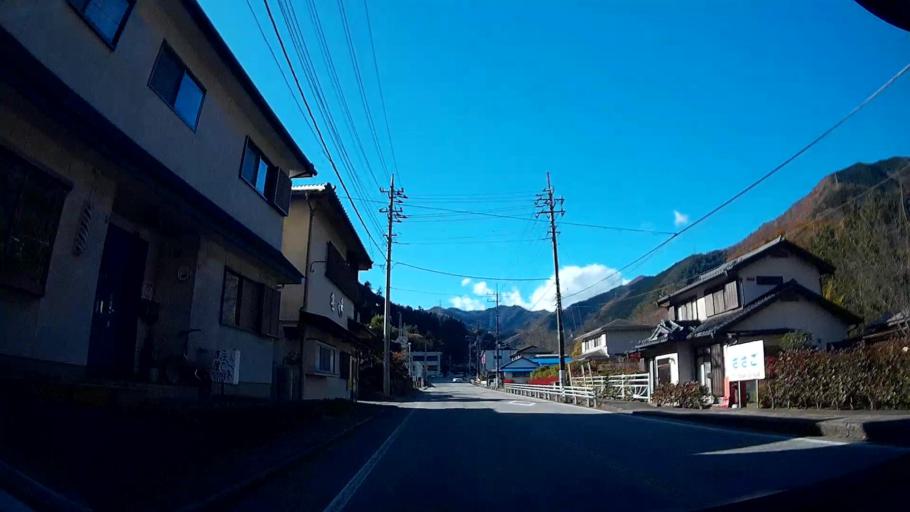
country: JP
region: Yamanashi
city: Otsuki
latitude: 35.6042
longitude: 138.8249
